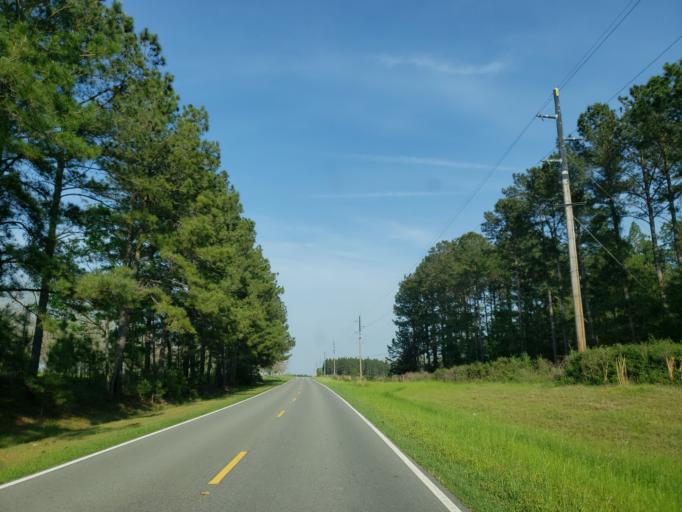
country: US
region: Georgia
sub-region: Tift County
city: Tifton
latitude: 31.5715
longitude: -83.5273
